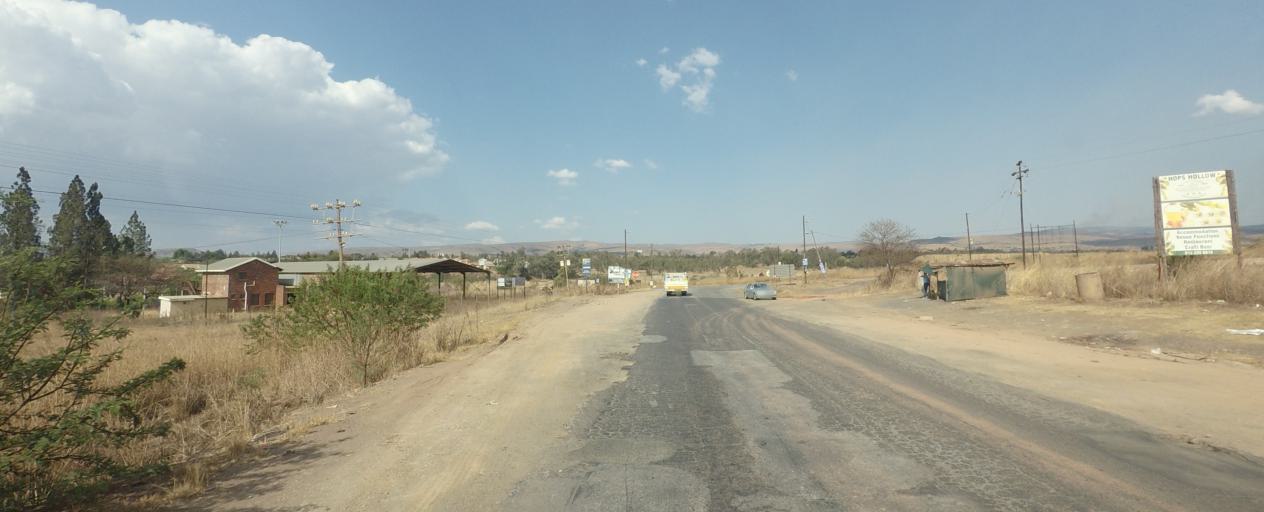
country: ZA
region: Mpumalanga
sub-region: Ehlanzeni District
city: Lydenburg
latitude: -25.1146
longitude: 30.4460
